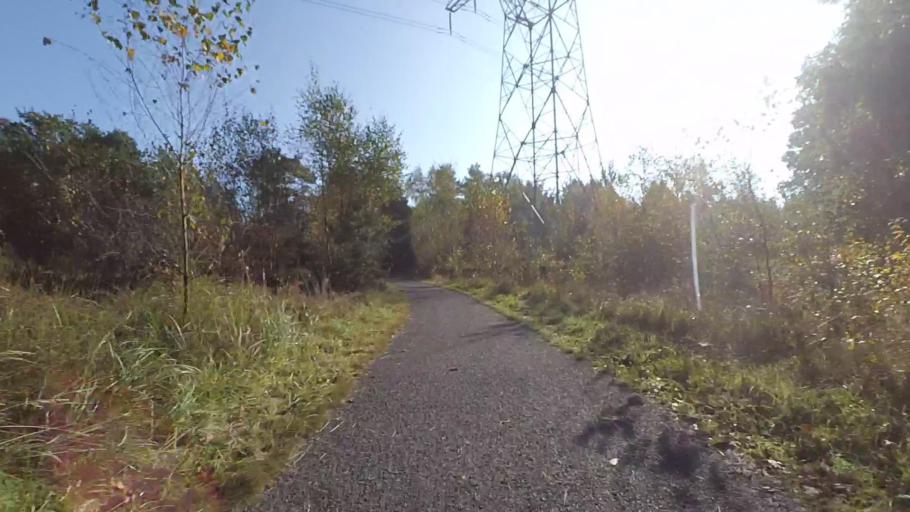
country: NL
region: Gelderland
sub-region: Gemeente Harderwijk
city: Harderwijk
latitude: 52.3371
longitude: 5.6523
